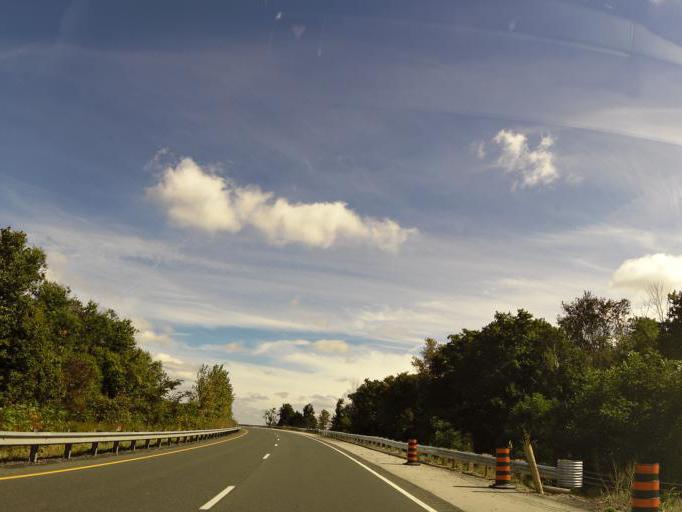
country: CA
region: Ontario
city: London
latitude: 42.9039
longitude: -81.2373
